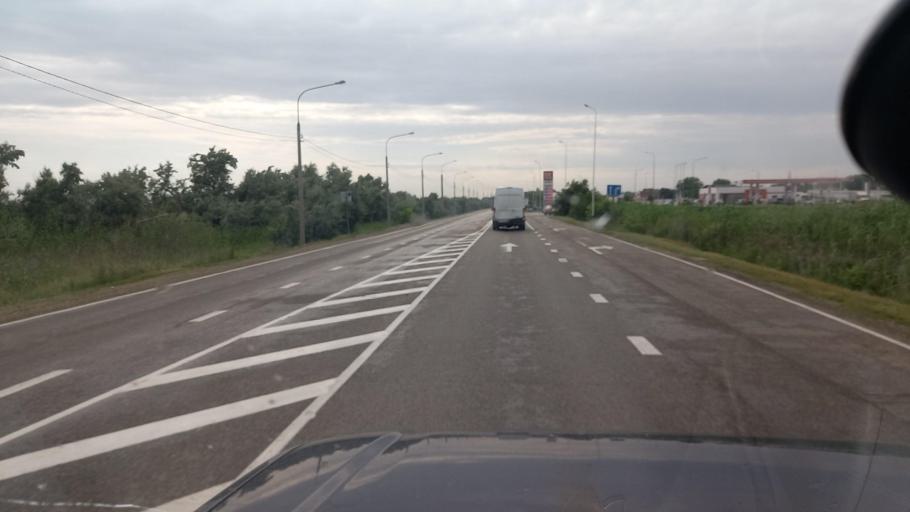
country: RU
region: Krasnodarskiy
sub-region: Taymyrsky Dolgano-Nenetsky District
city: Golubitskaya
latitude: 45.3159
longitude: 37.2956
